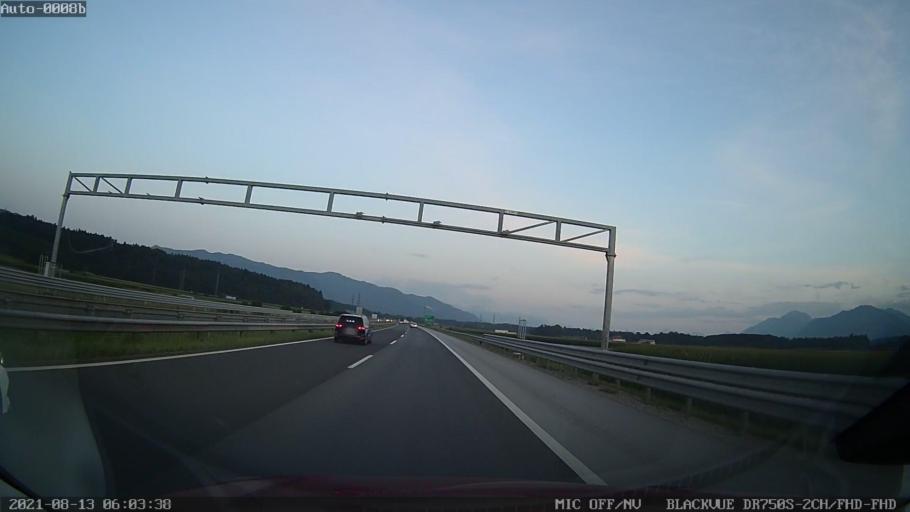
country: SI
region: Naklo
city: Naklo
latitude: 46.2782
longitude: 14.3120
